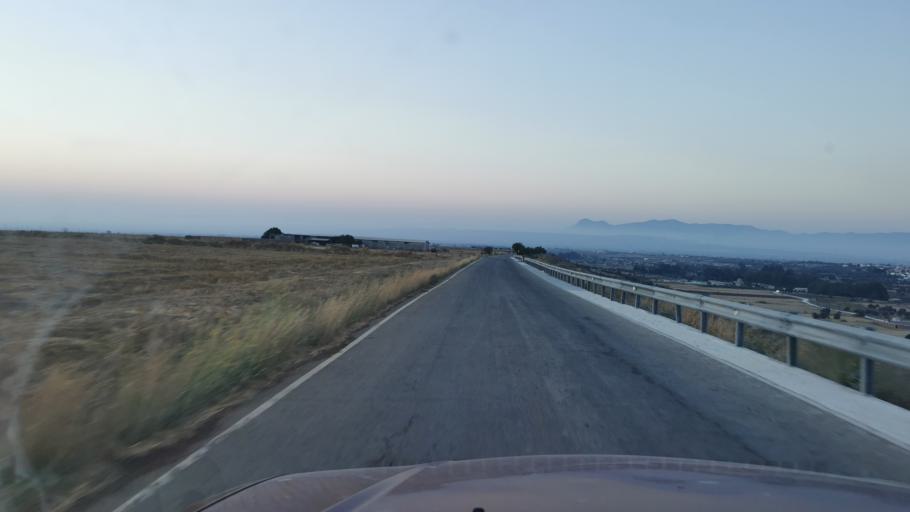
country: CY
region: Lefkosia
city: Peristerona
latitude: 35.0892
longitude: 33.0821
